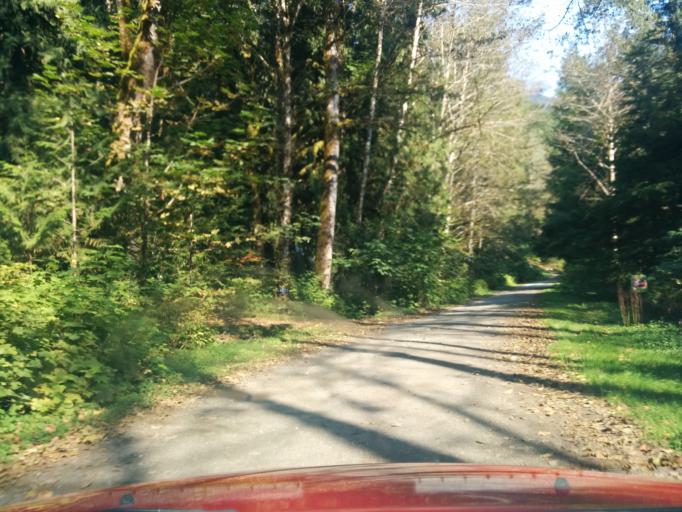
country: US
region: Washington
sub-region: Snohomish County
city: Darrington
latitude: 48.5213
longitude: -121.3526
